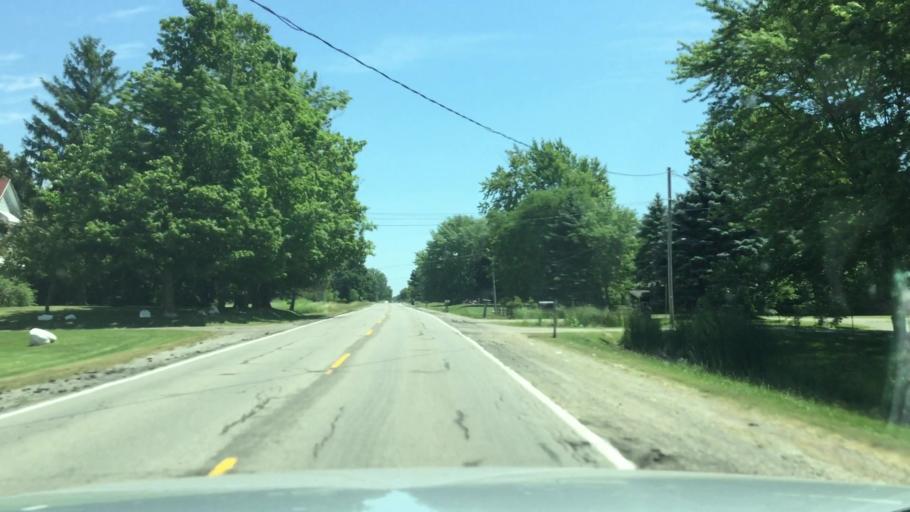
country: US
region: Michigan
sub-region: Genesee County
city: Swartz Creek
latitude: 42.9427
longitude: -83.8088
